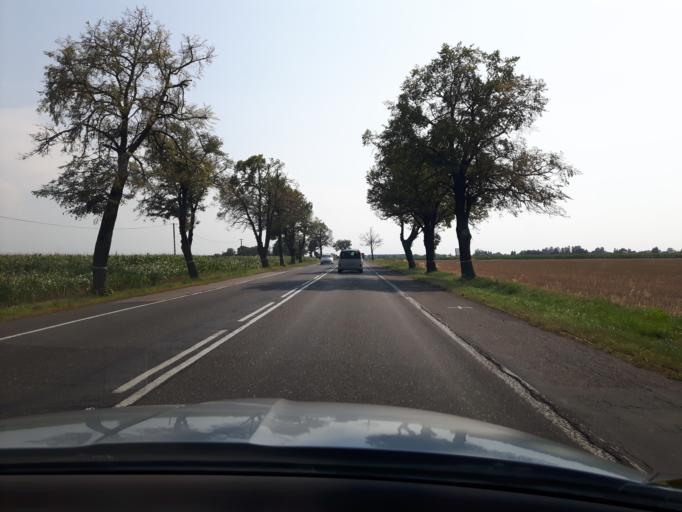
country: PL
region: Masovian Voivodeship
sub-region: Powiat plonski
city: Plonsk
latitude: 52.6462
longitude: 20.3739
